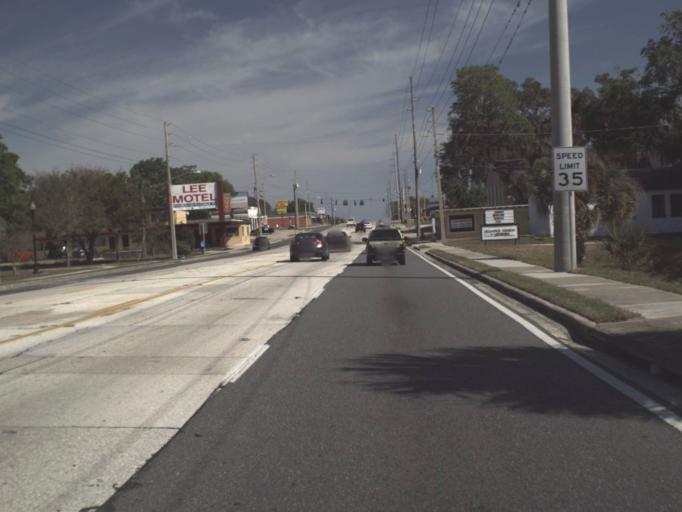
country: US
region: Florida
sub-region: Lake County
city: Leesburg
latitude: 28.8089
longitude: -81.8875
